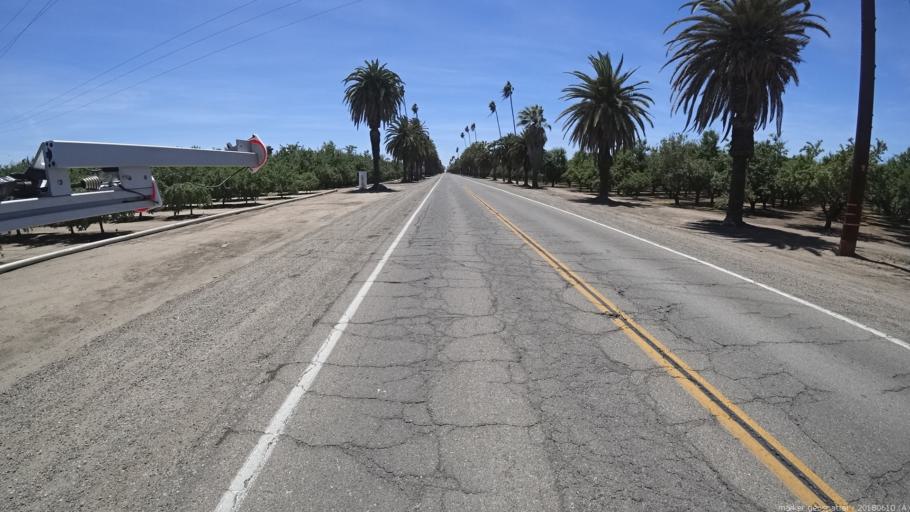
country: US
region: California
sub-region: Madera County
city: Chowchilla
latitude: 37.0688
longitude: -120.3100
